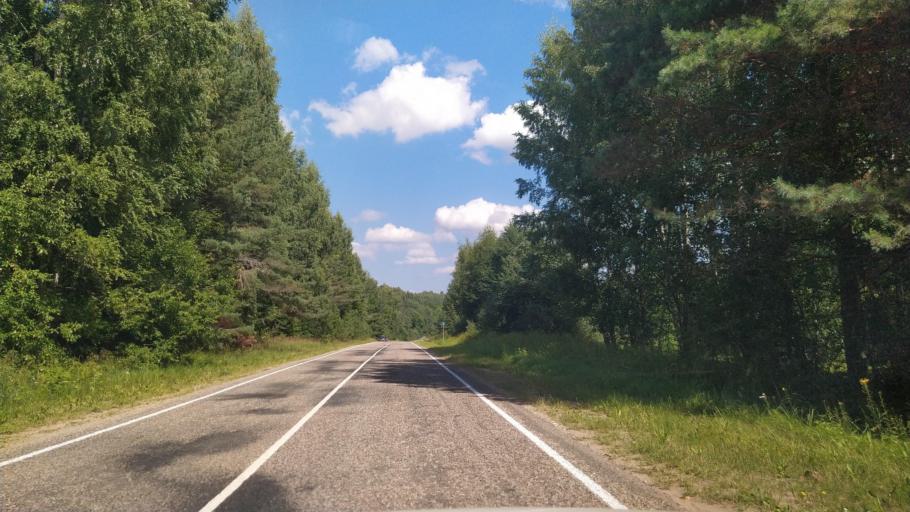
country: RU
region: Pskov
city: Pushkinskiye Gory
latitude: 57.0605
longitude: 28.9476
